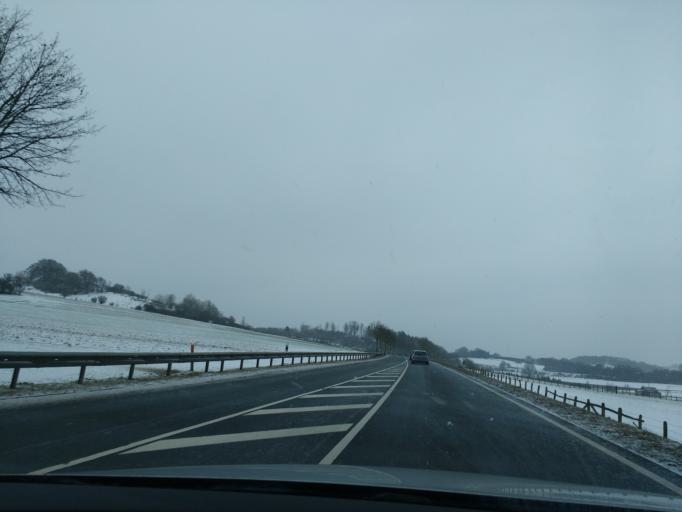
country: DE
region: North Rhine-Westphalia
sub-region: Regierungsbezirk Arnsberg
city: Brilon
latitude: 51.4024
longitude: 8.5994
